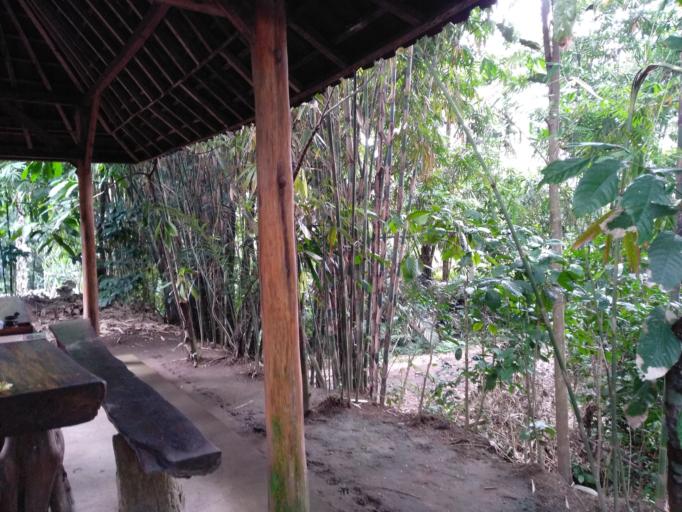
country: ID
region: Bali
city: Banjar Taro Kelod
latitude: -8.3585
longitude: 115.3012
